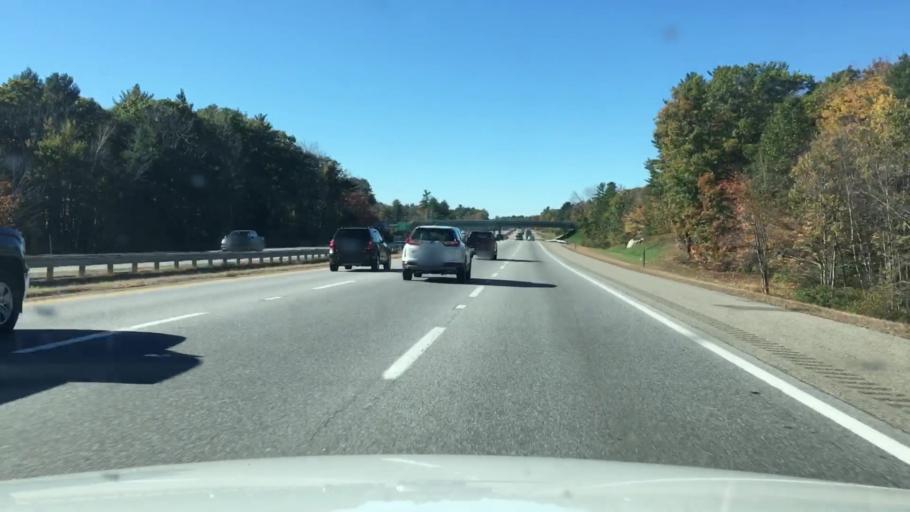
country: US
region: Maine
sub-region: York County
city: Biddeford
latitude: 43.4702
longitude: -70.5124
